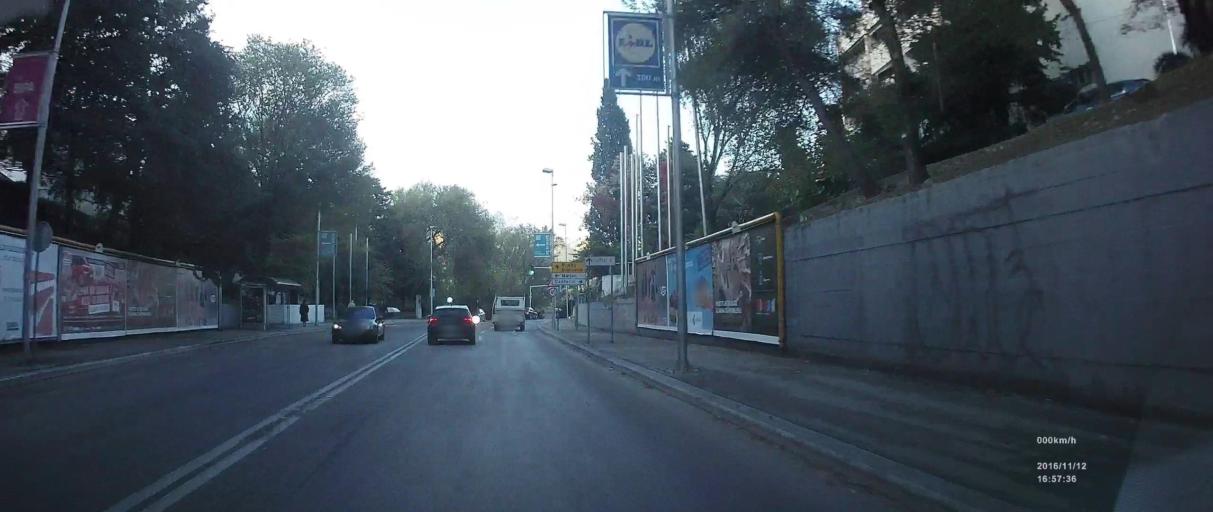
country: HR
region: Splitsko-Dalmatinska
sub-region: Grad Split
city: Split
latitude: 43.5128
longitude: 16.4278
